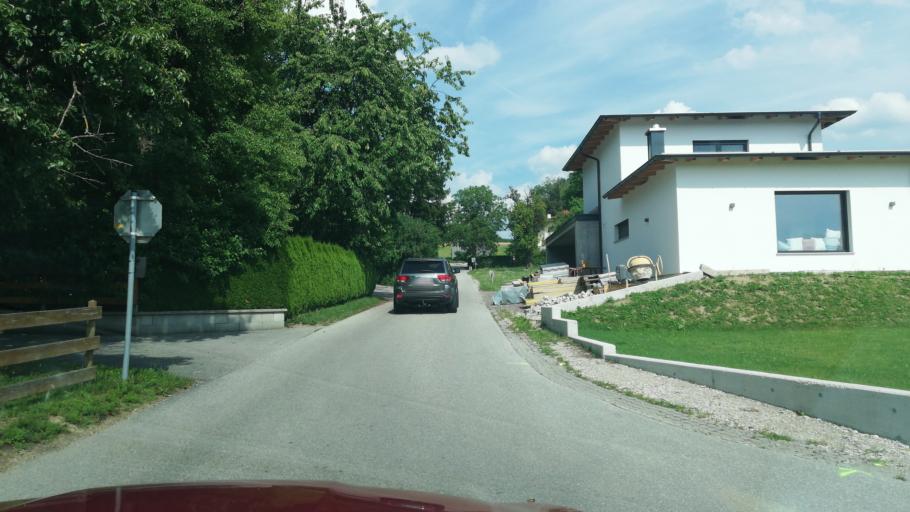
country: AT
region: Upper Austria
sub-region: Politischer Bezirk Vocklabruck
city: Puhret
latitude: 48.0352
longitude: 13.7033
